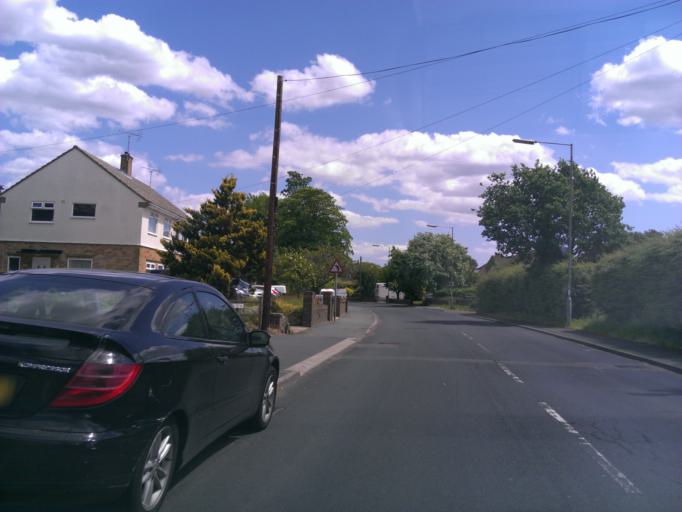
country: GB
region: England
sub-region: Essex
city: Colchester
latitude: 51.8707
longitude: 0.9221
